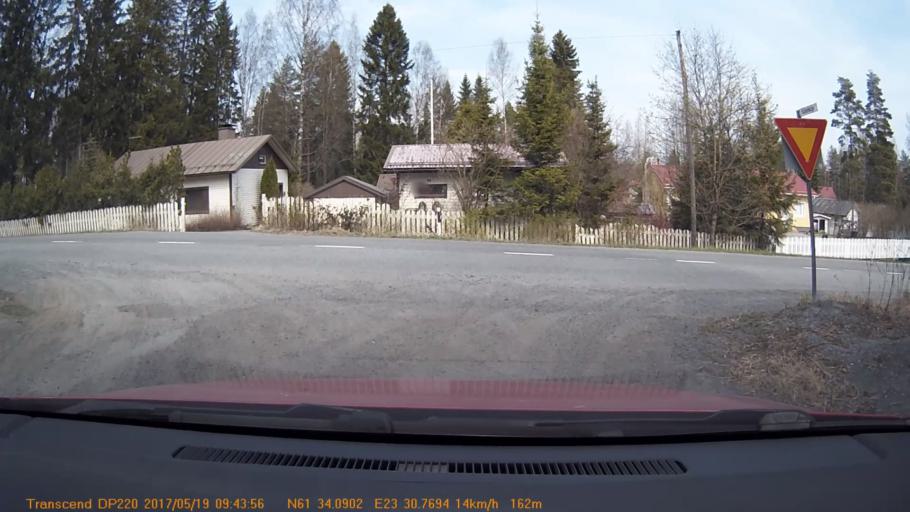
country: FI
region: Pirkanmaa
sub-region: Tampere
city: Yloejaervi
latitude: 61.5680
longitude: 23.5128
